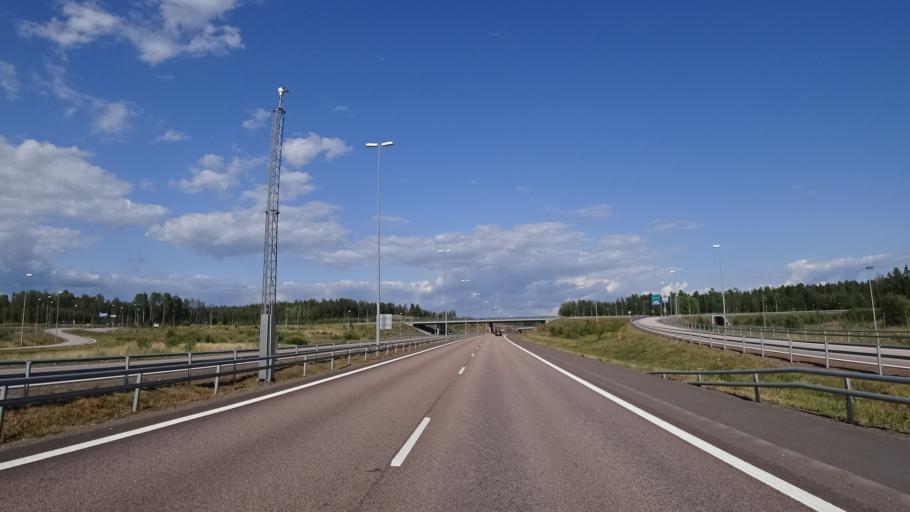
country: FI
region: Kymenlaakso
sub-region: Kotka-Hamina
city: Hamina
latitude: 60.5845
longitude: 27.1501
